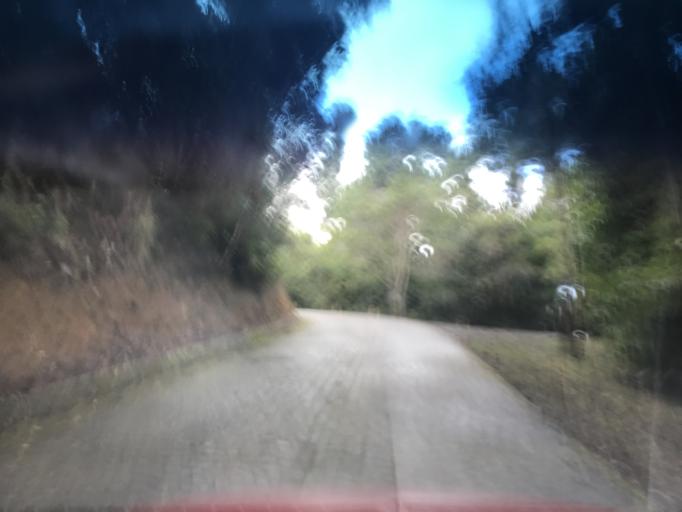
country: BR
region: Bahia
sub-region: Gandu
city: Gandu
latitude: -13.9057
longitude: -39.4612
